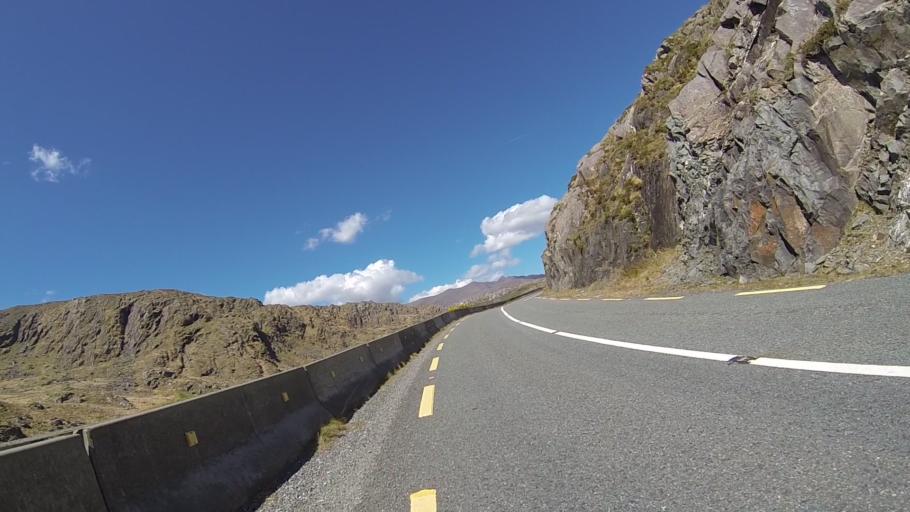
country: IE
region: Munster
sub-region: Ciarrai
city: Kenmare
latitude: 51.9335
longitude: -9.6525
